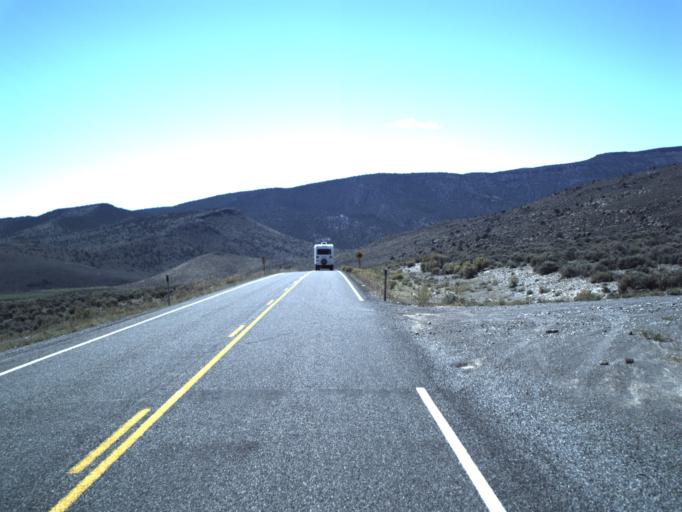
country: US
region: Utah
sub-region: Piute County
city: Junction
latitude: 38.1781
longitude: -112.0216
